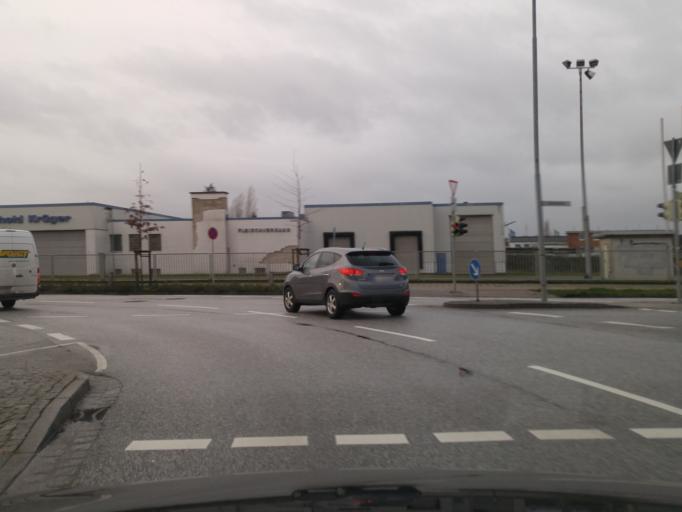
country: DE
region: Schleswig-Holstein
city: Luebeck
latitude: 53.8845
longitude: 10.6907
